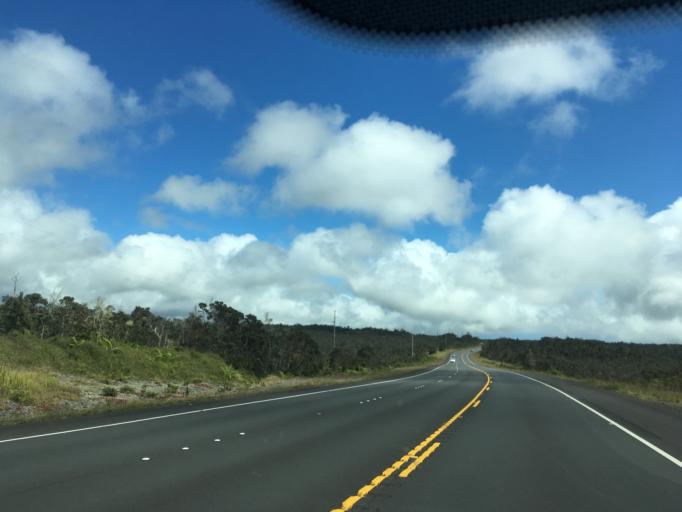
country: US
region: Hawaii
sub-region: Hawaii County
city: Wainaku
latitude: 19.6770
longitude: -155.3179
